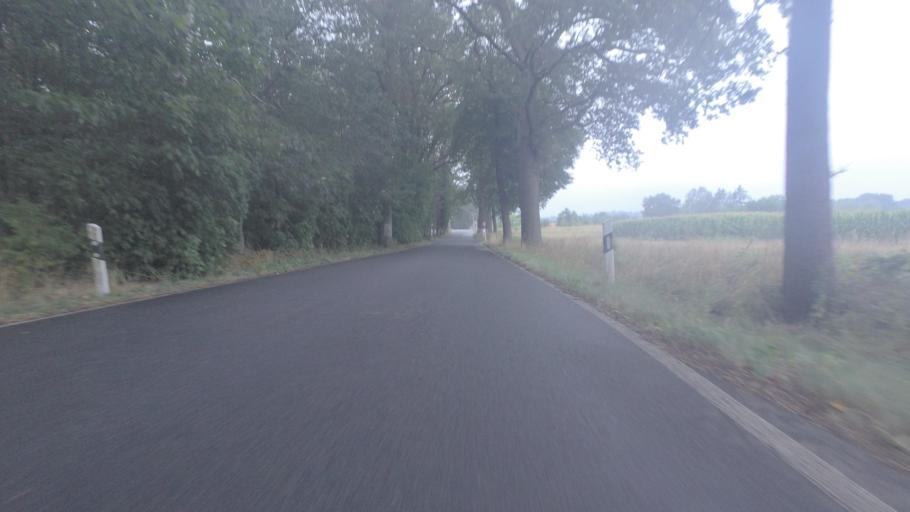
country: DE
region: Brandenburg
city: Heiligengrabe
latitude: 53.1518
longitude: 12.3436
